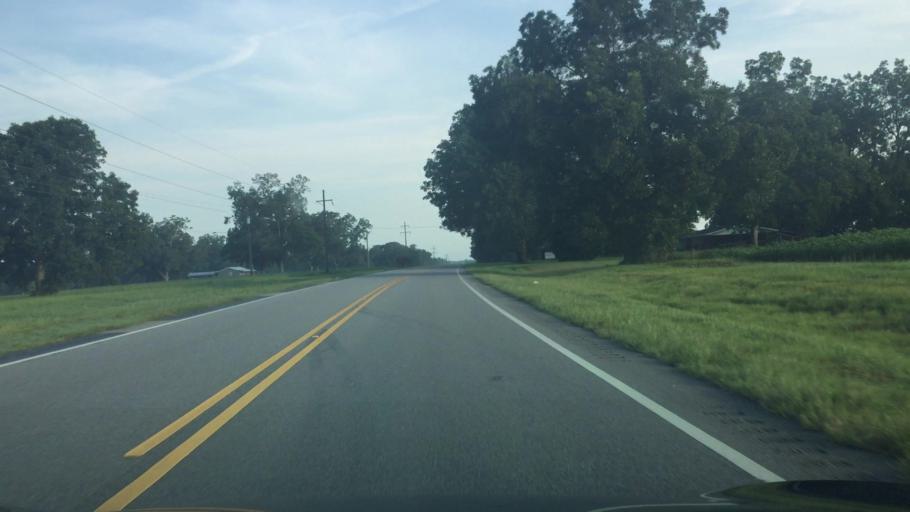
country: US
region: Alabama
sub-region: Covington County
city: Florala
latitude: 31.0483
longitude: -86.3865
